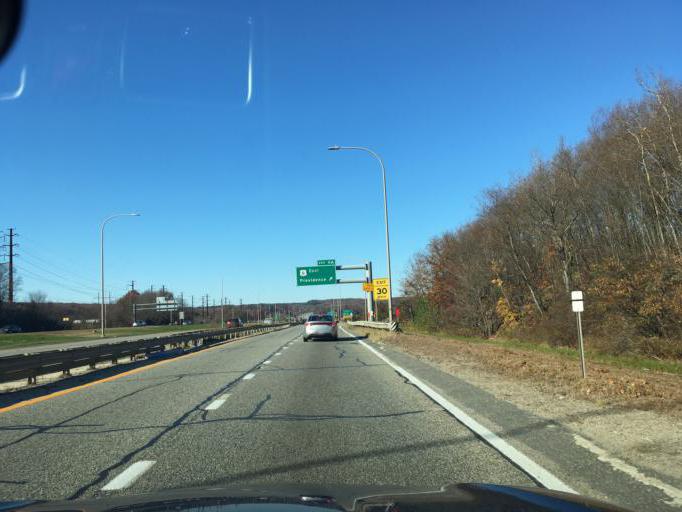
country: US
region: Rhode Island
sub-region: Providence County
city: Johnston
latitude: 41.8168
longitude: -71.5104
